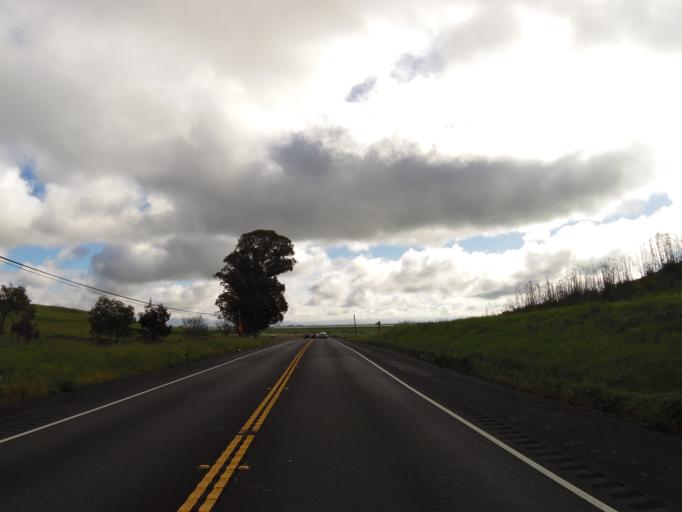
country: US
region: California
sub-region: Marin County
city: Black Point-Green Point
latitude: 38.1762
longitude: -122.4509
